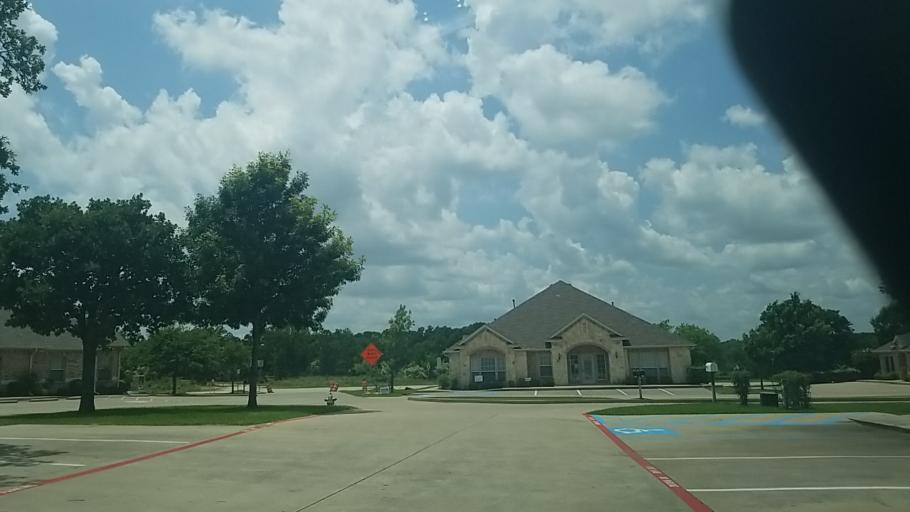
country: US
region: Texas
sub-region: Denton County
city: Denton
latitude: 33.1716
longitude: -97.1117
